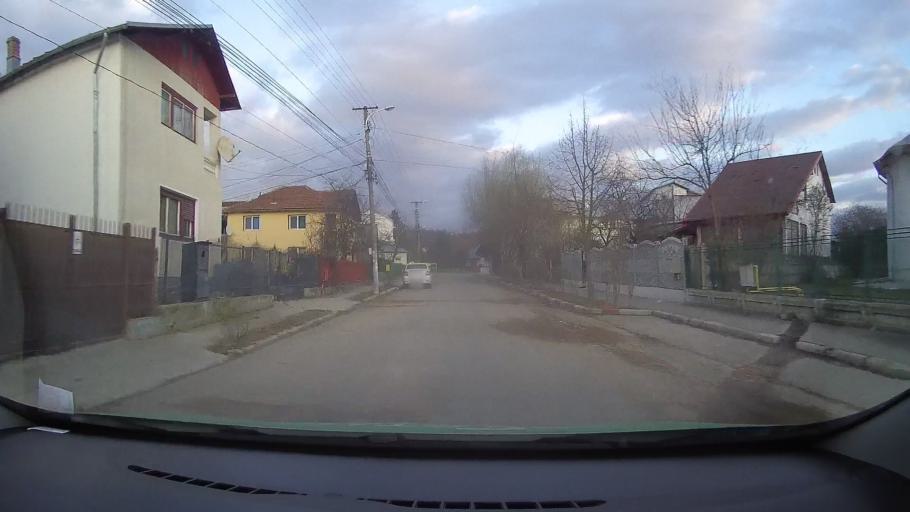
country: RO
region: Dambovita
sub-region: Municipiul Moreni
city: Moreni
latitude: 44.9927
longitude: 25.6436
